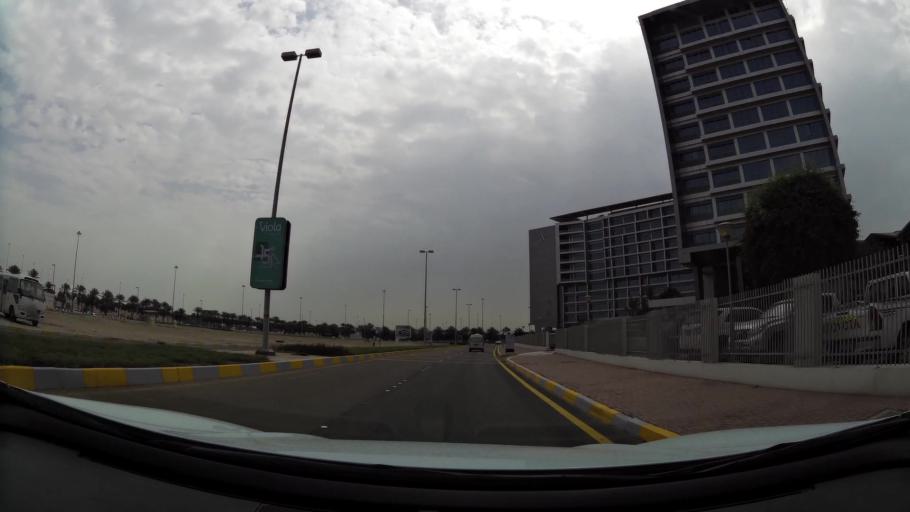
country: AE
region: Abu Dhabi
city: Abu Dhabi
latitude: 24.4250
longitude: 54.4734
